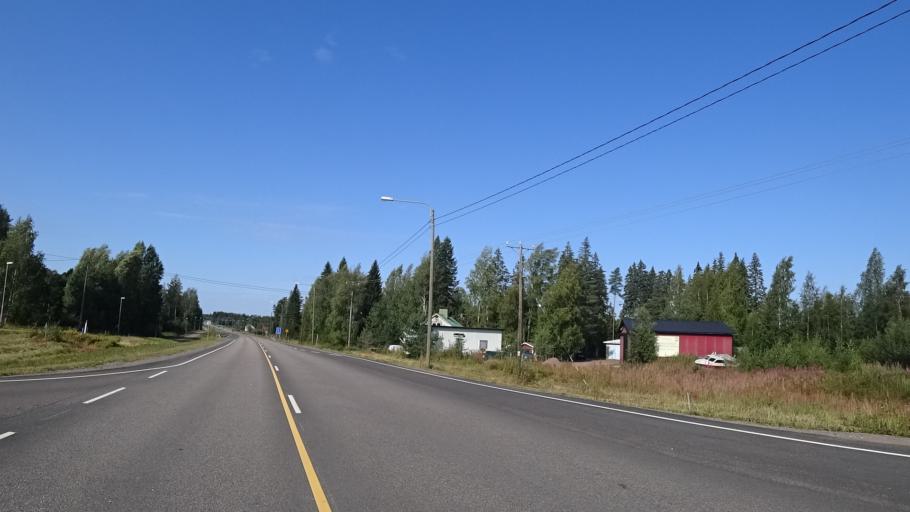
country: FI
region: Kymenlaakso
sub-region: Kotka-Hamina
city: Virojoki
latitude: 60.5931
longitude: 27.7625
